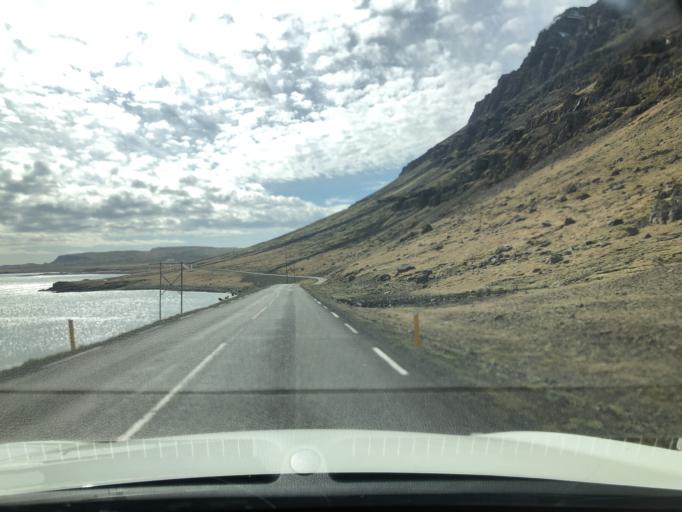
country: IS
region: East
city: Reydarfjoerdur
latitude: 64.7093
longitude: -14.3975
